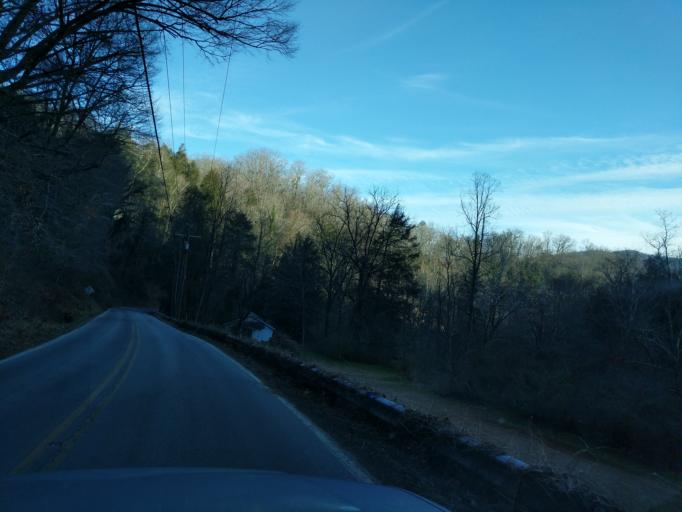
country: US
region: North Carolina
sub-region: Henderson County
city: Edneyville
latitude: 35.4572
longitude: -82.2997
